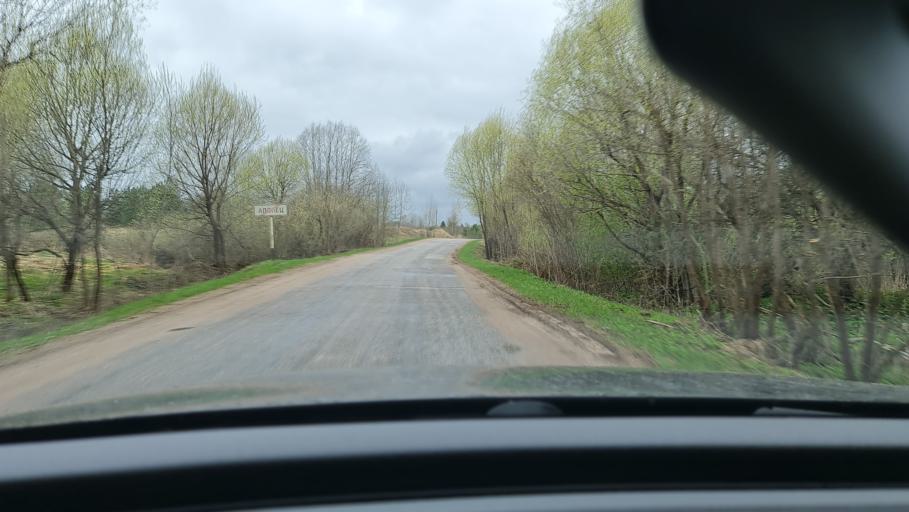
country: RU
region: Novgorod
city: Marevo
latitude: 57.1085
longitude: 31.7801
